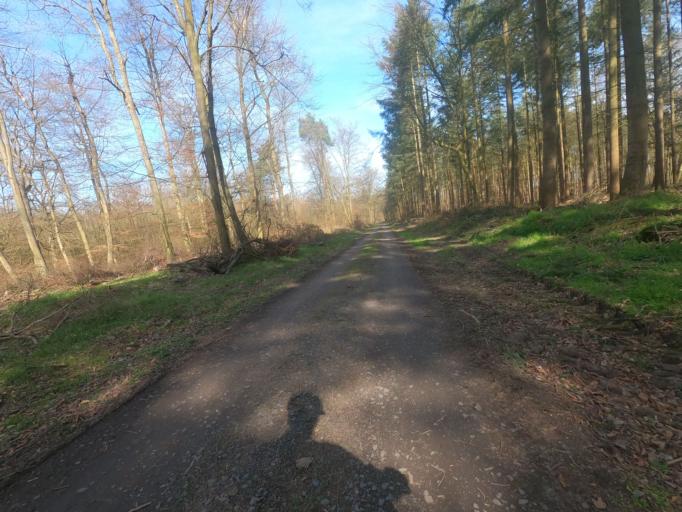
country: DE
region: Hesse
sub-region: Regierungsbezirk Darmstadt
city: Buttelborn
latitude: 49.9445
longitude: 8.5383
